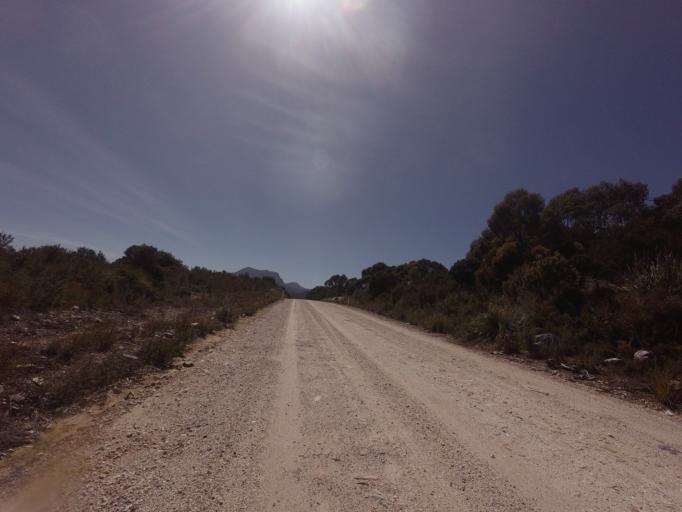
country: AU
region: Tasmania
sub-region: Huon Valley
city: Geeveston
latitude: -43.0285
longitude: 146.3512
